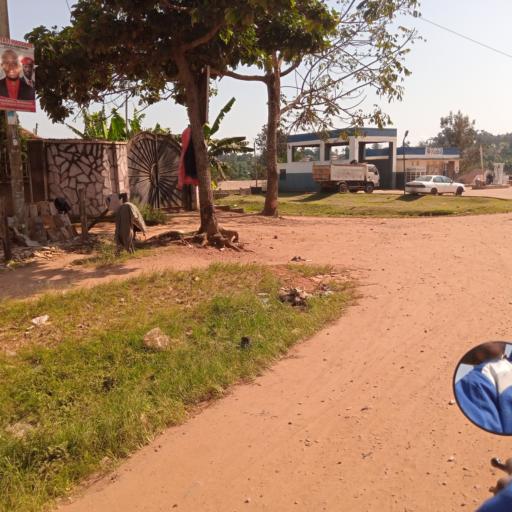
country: UG
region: Central Region
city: Masaka
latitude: -0.3444
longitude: 31.7288
